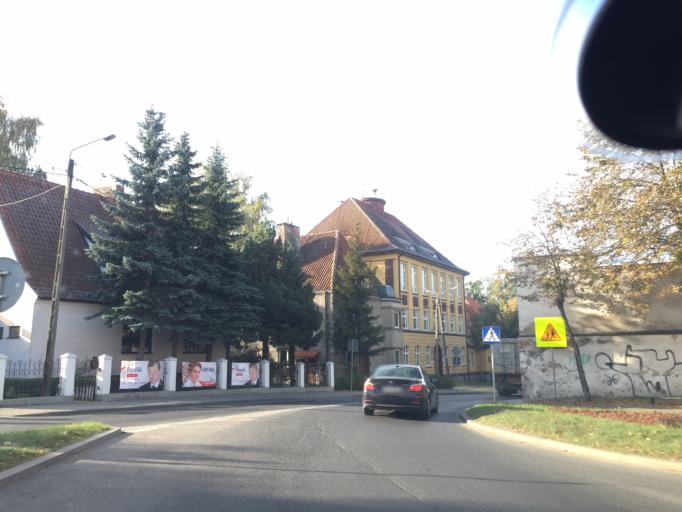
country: PL
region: Warmian-Masurian Voivodeship
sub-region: Powiat lidzbarski
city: Lidzbark Warminski
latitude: 54.1254
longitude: 20.5875
